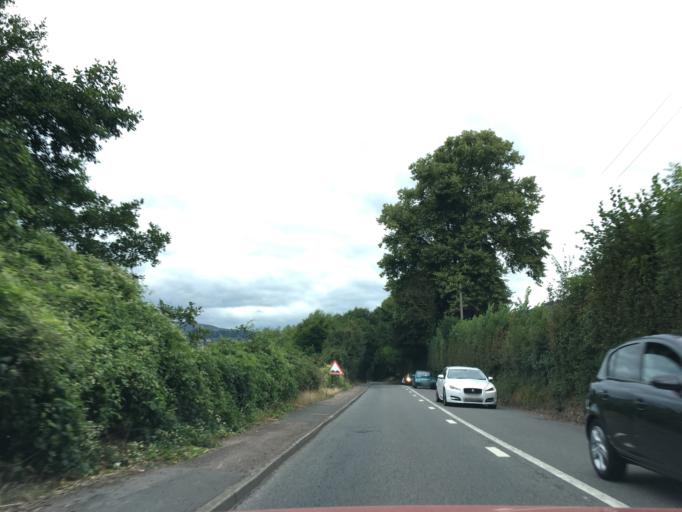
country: GB
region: Wales
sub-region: Monmouthshire
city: Abergavenny
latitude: 51.8324
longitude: -3.0499
